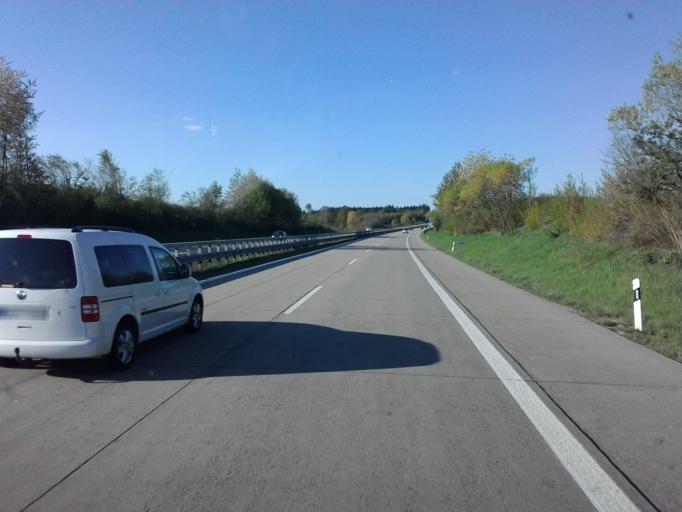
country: DE
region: Baden-Wuerttemberg
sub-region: Regierungsbezirk Stuttgart
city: Ellwangen
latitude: 48.9691
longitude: 10.1865
